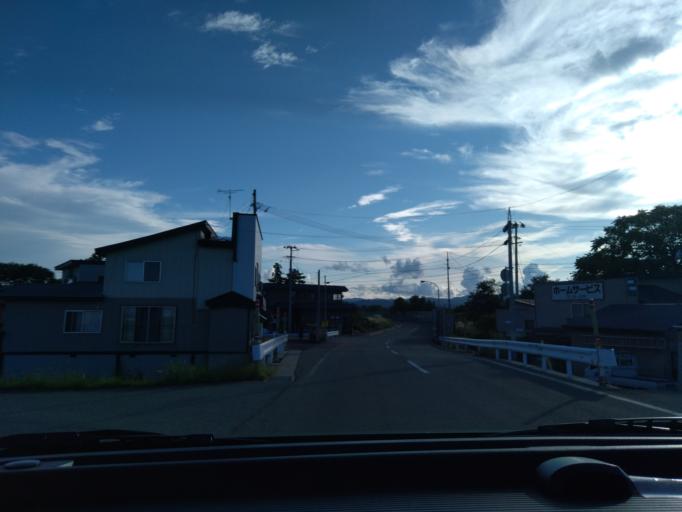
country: JP
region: Akita
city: Omagari
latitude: 39.4129
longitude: 140.4837
